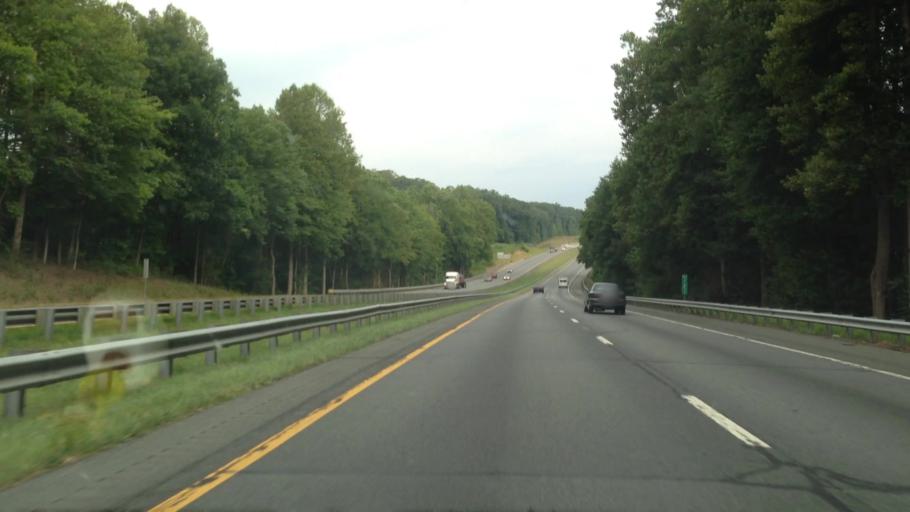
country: US
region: North Carolina
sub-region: Forsyth County
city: Tobaccoville
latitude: 36.2367
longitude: -80.3391
